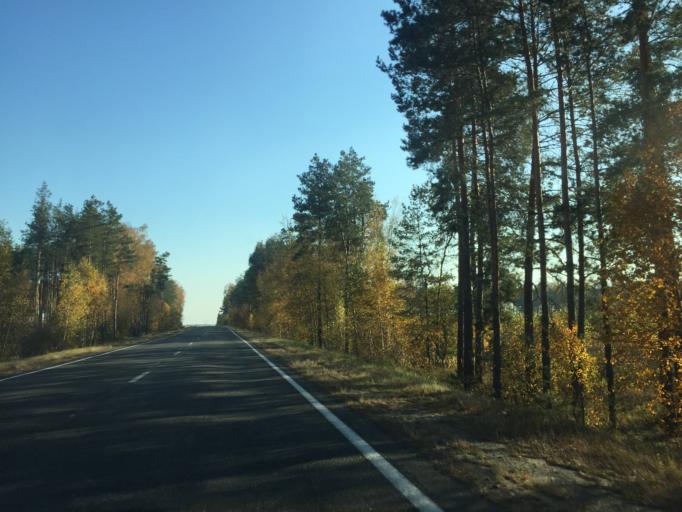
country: BY
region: Gomel
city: Dobrush
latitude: 52.3317
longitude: 31.2386
